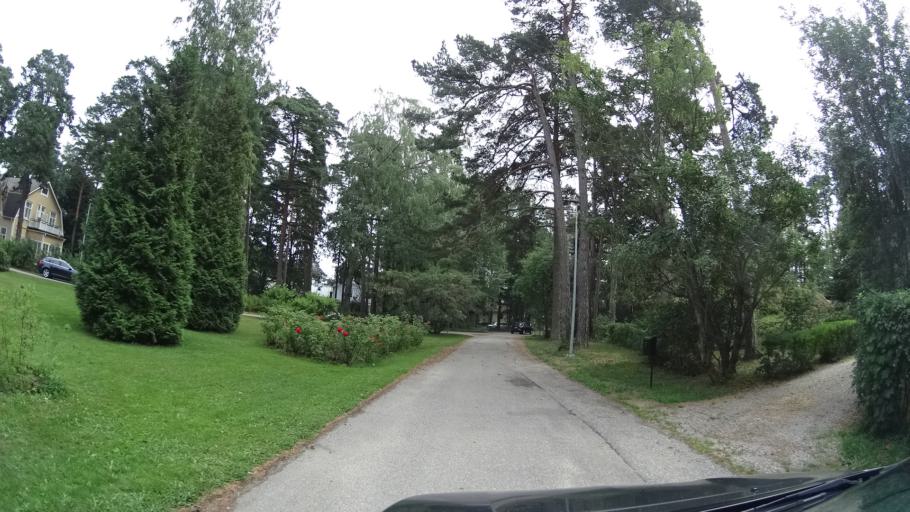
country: FI
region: Uusimaa
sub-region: Raaseporin
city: Hanko
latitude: 59.8280
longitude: 22.9845
